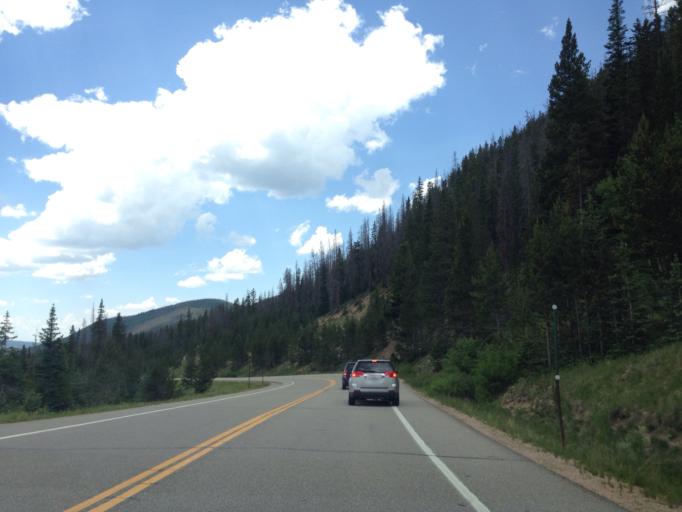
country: US
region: Colorado
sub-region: Larimer County
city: Estes Park
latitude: 40.5046
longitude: -105.9054
